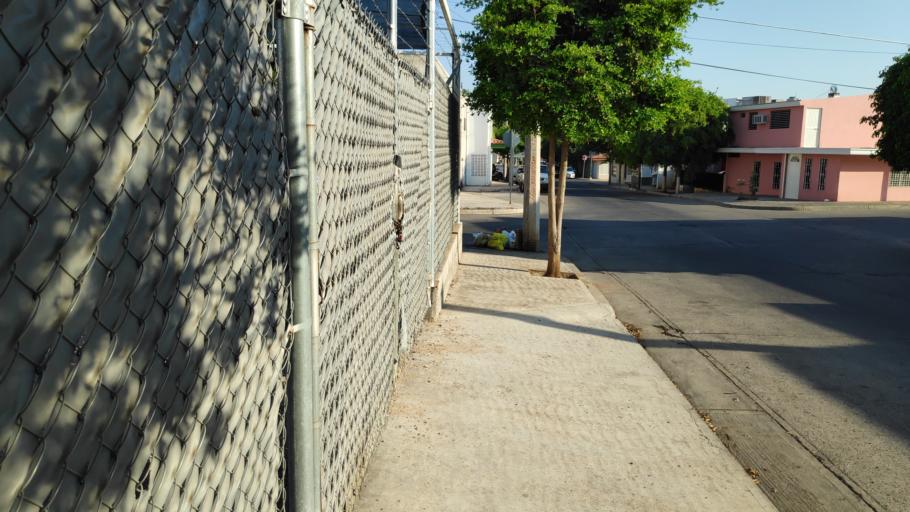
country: MX
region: Sinaloa
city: Culiacan
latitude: 24.7905
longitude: -107.4041
